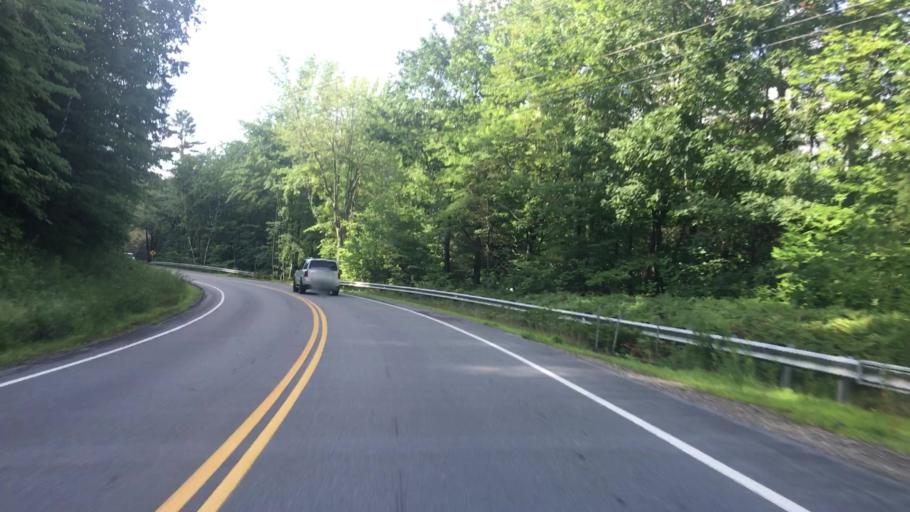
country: US
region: New Hampshire
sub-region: Belknap County
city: Gilford
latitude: 43.5609
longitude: -71.3951
